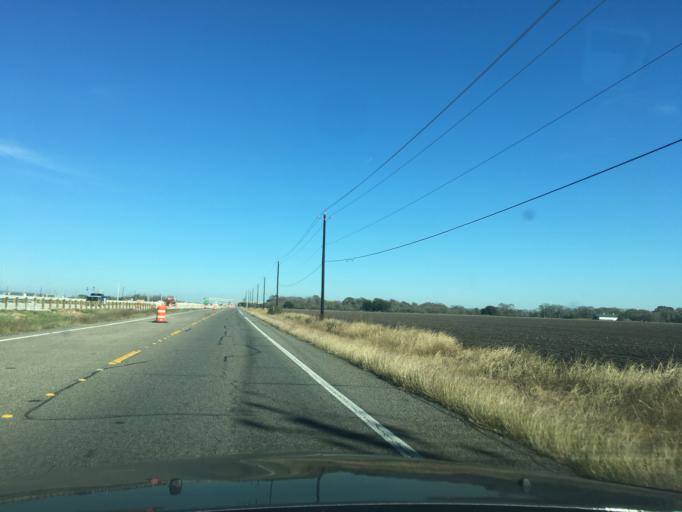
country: US
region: Texas
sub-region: Wharton County
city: East Bernard
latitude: 29.4629
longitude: -95.9733
